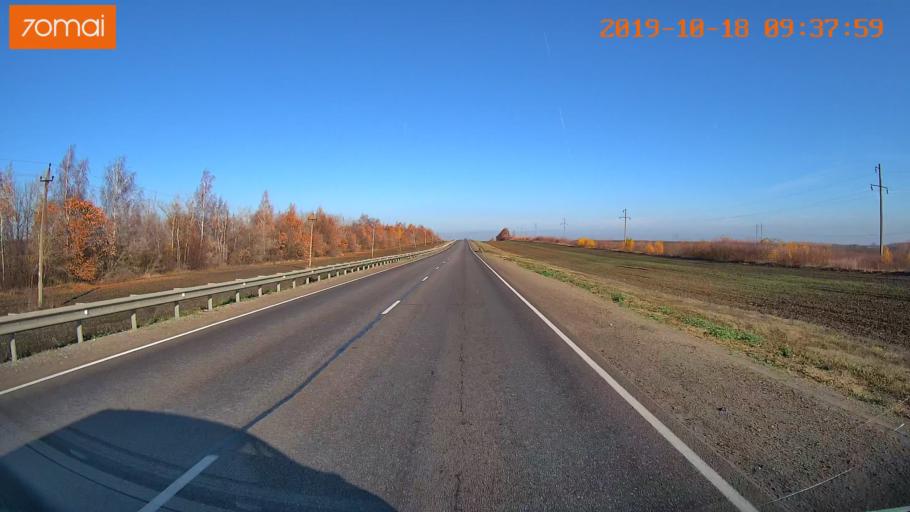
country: RU
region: Tula
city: Yefremov
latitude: 53.2309
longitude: 38.1388
